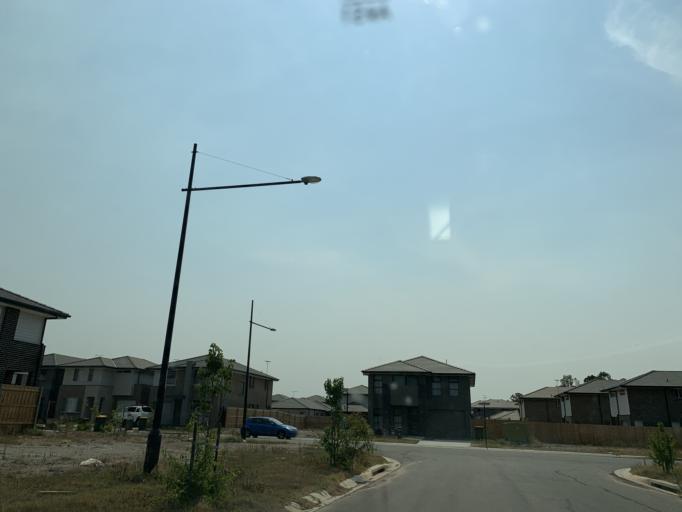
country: AU
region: New South Wales
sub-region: Blacktown
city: Blackett
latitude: -33.7125
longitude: 150.8205
